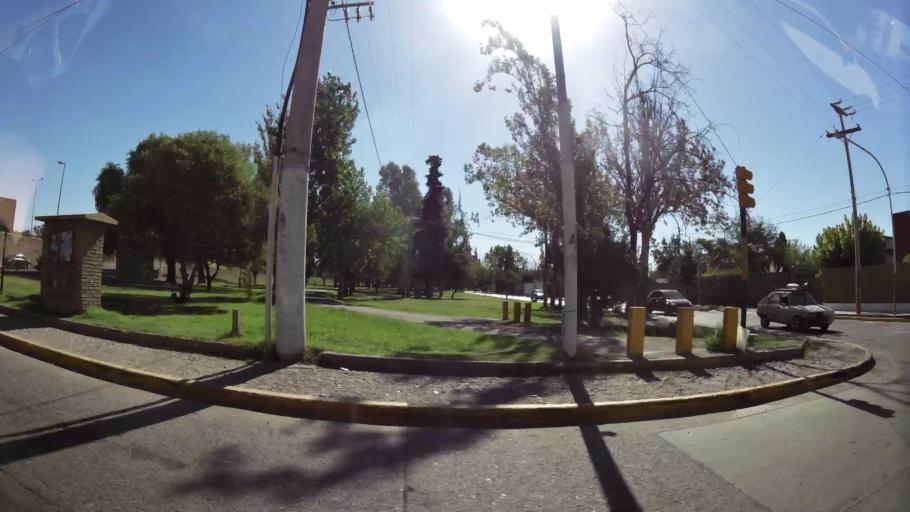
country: AR
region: Mendoza
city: Villa Nueva
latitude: -32.9058
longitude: -68.7898
